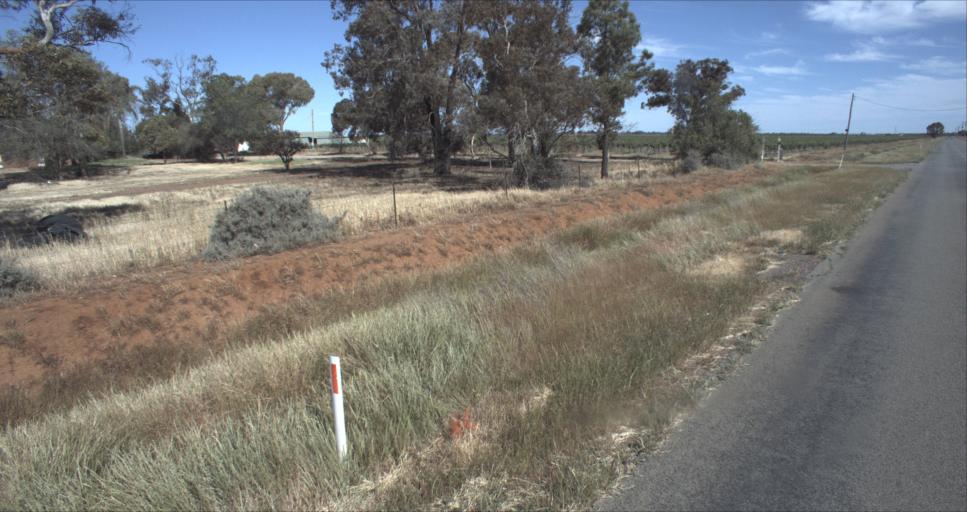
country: AU
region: New South Wales
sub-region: Leeton
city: Leeton
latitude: -34.5731
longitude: 146.3813
